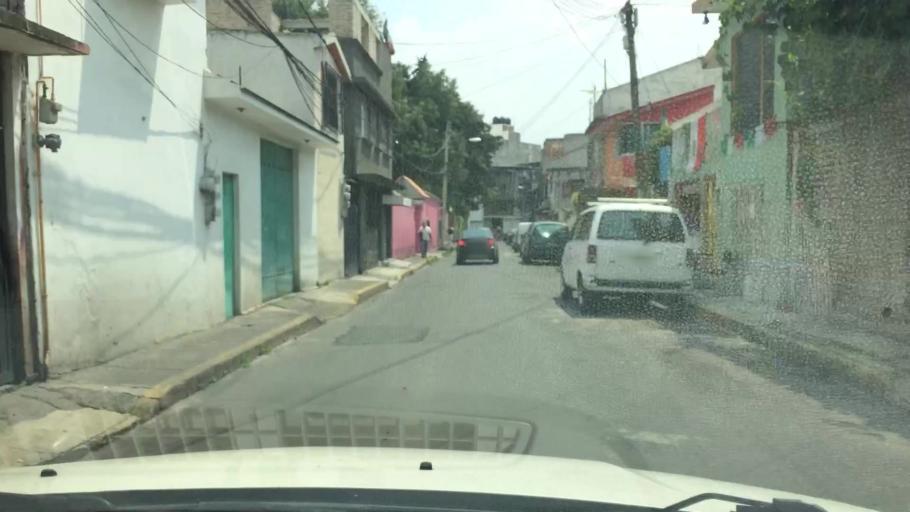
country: MX
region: Mexico City
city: Xochimilco
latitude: 19.2731
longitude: -99.1295
